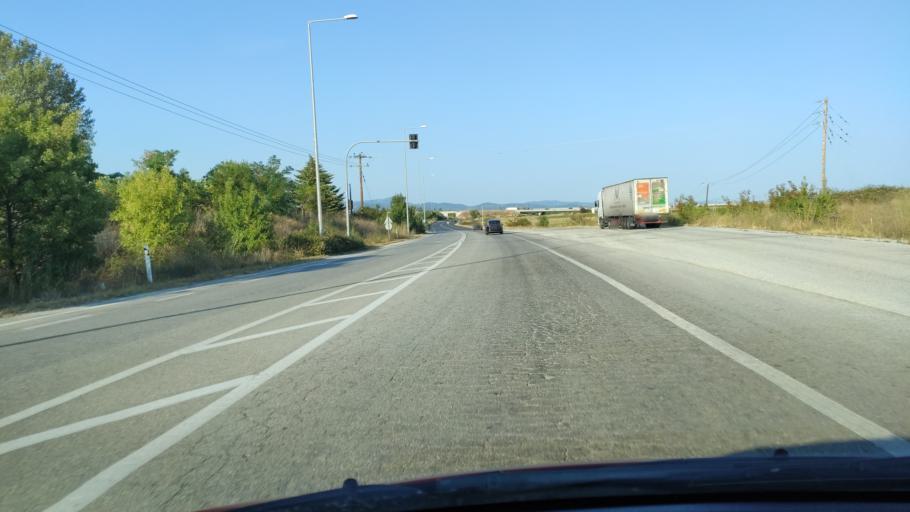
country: GR
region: East Macedonia and Thrace
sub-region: Nomos Rodopis
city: Komotini
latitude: 41.1049
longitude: 25.3332
